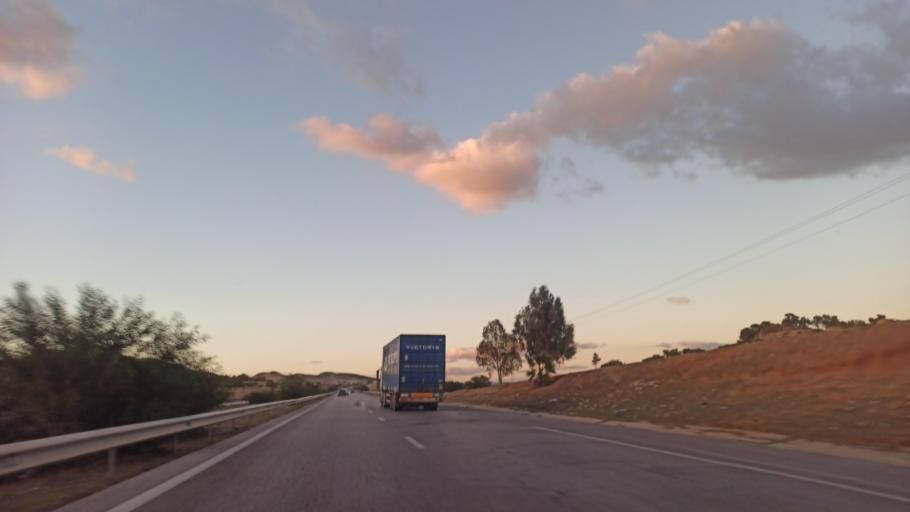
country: TN
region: Susah
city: Harqalah
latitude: 36.2220
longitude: 10.4170
